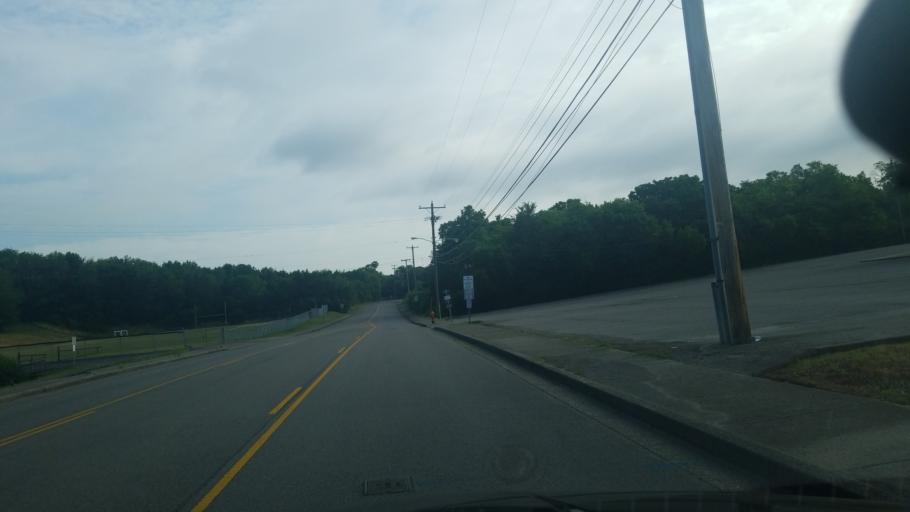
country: US
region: Tennessee
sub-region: Davidson County
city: Nashville
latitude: 36.2335
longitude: -86.7507
